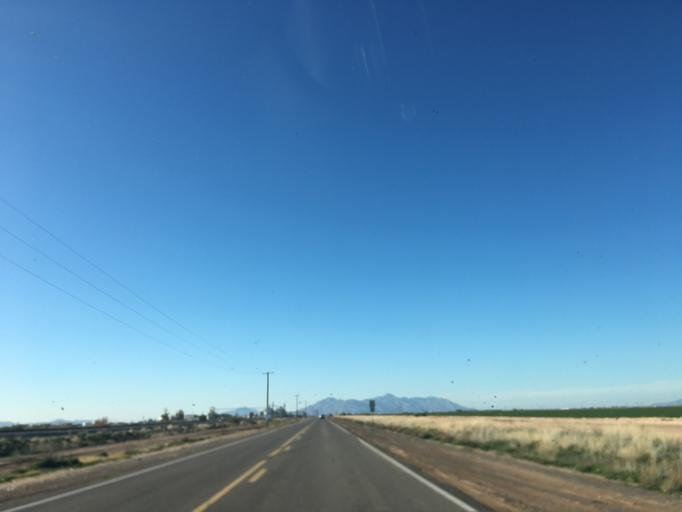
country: US
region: Arizona
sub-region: Pinal County
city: Maricopa
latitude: 33.0046
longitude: -111.9635
